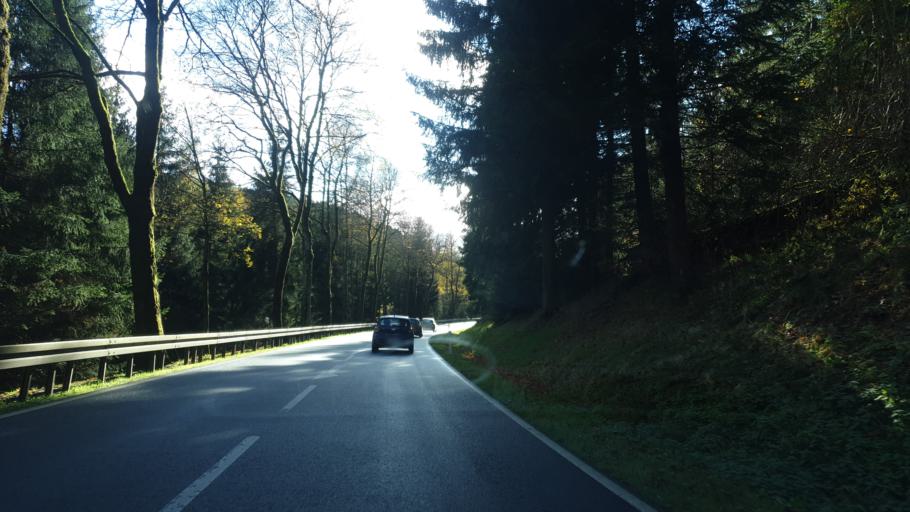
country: DE
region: Saxony
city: Sosa
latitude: 50.5251
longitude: 12.6418
